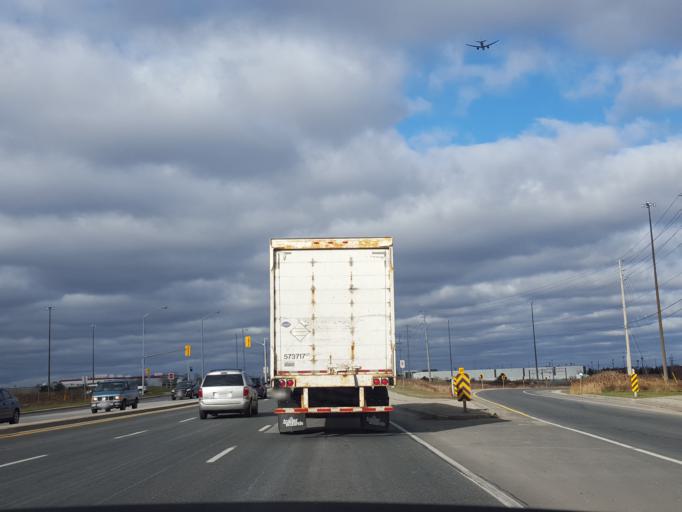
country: CA
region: Ontario
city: Brampton
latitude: 43.7248
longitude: -79.6704
